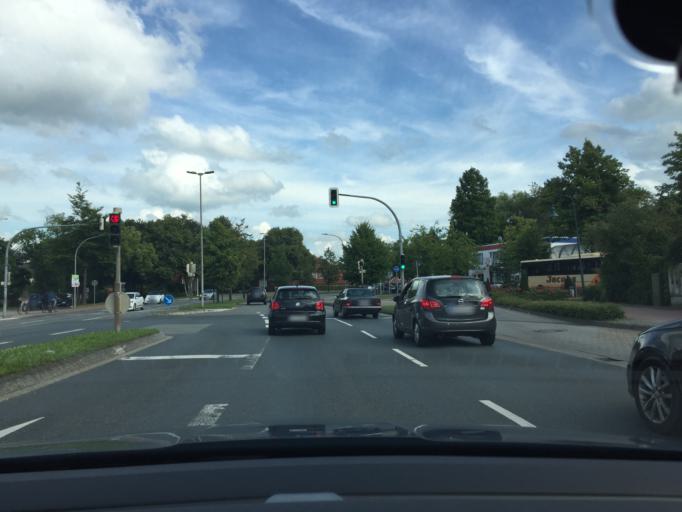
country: DE
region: Lower Saxony
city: Aurich
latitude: 53.4723
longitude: 7.4839
